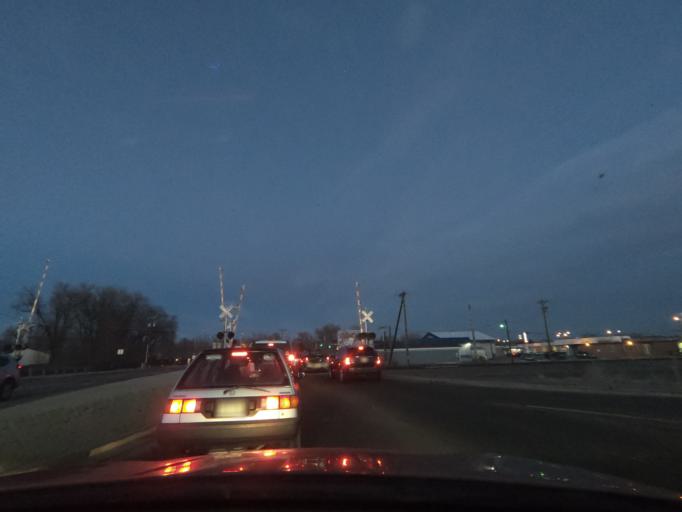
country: US
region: Colorado
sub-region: El Paso County
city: Security-Widefield
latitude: 38.7368
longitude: -104.7306
